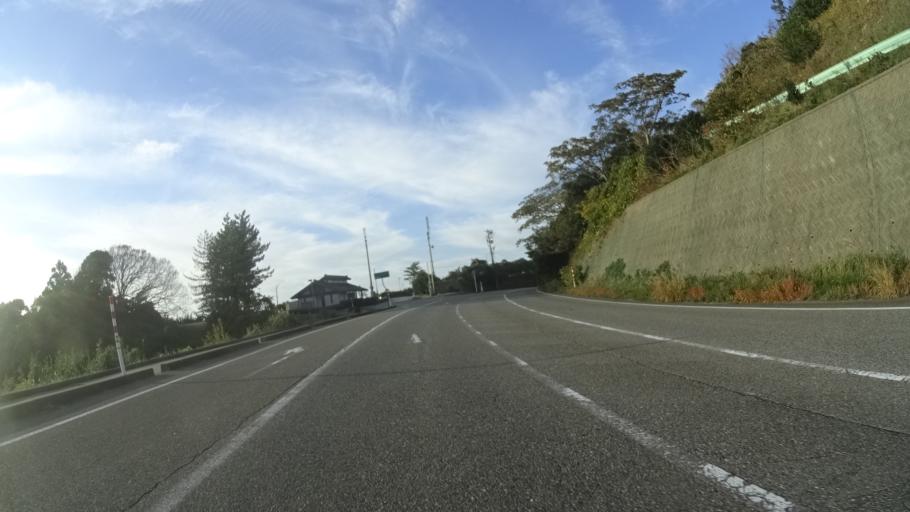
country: JP
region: Ishikawa
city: Hakui
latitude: 37.1005
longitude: 136.7305
